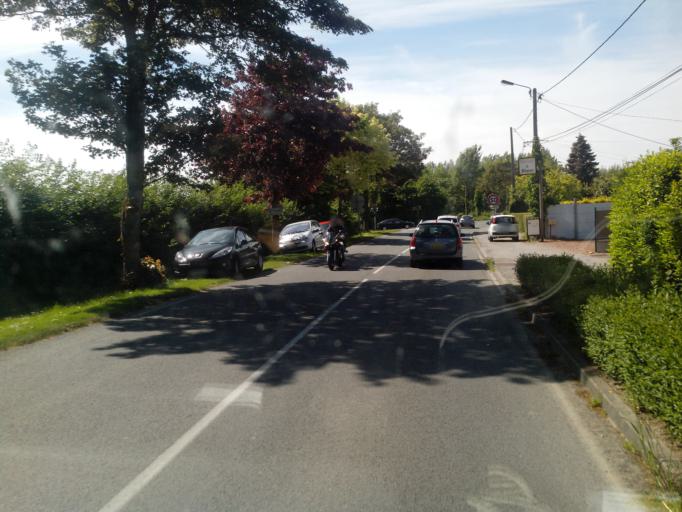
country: FR
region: Nord-Pas-de-Calais
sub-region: Departement du Pas-de-Calais
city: Saint-Josse
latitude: 50.4968
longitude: 1.7004
